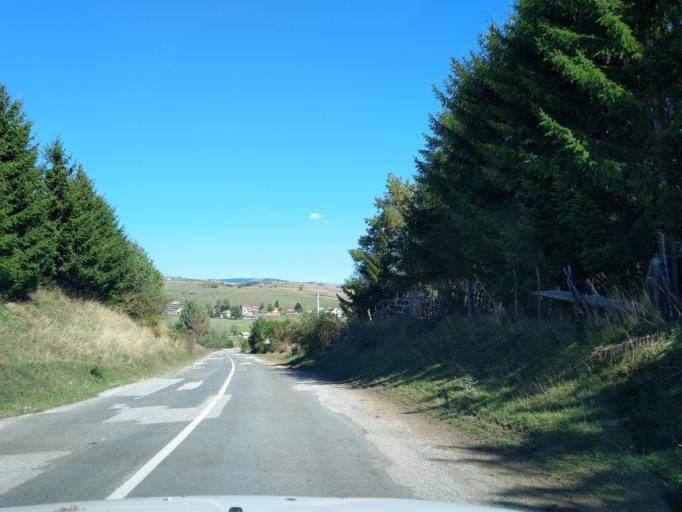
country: RS
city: Sokolovica
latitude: 43.2741
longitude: 20.1890
